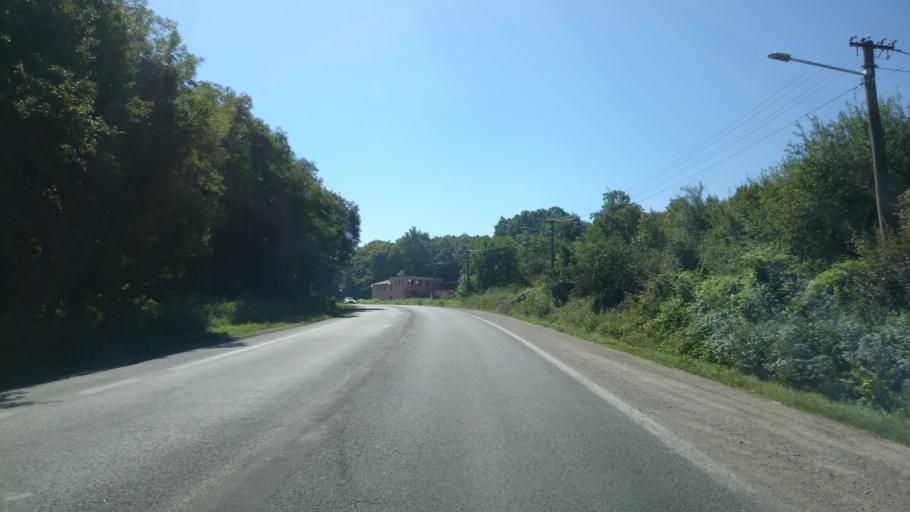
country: SK
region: Trenciansky
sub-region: Okres Trencin
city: Trencin
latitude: 48.8139
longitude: 18.0861
